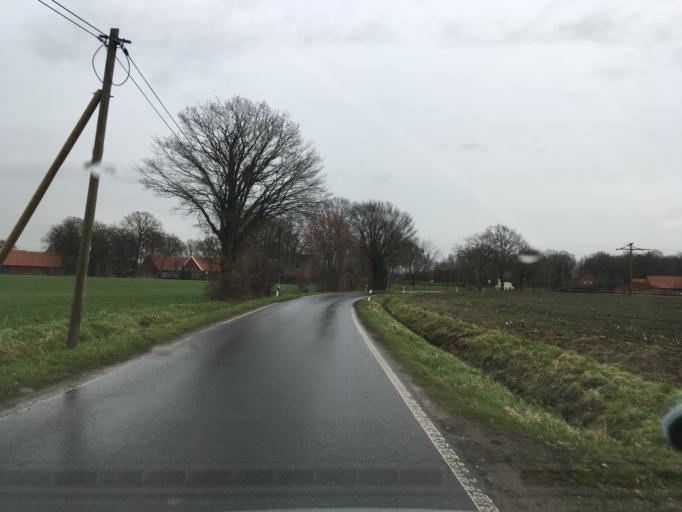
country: DE
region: North Rhine-Westphalia
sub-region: Regierungsbezirk Munster
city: Heek
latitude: 52.1378
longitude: 7.1163
